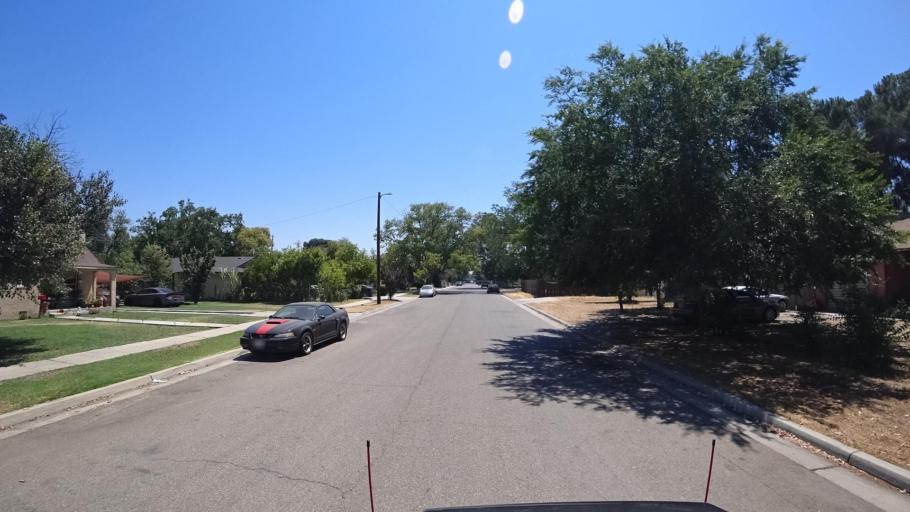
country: US
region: California
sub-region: Fresno County
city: Fresno
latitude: 36.7668
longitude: -119.7757
